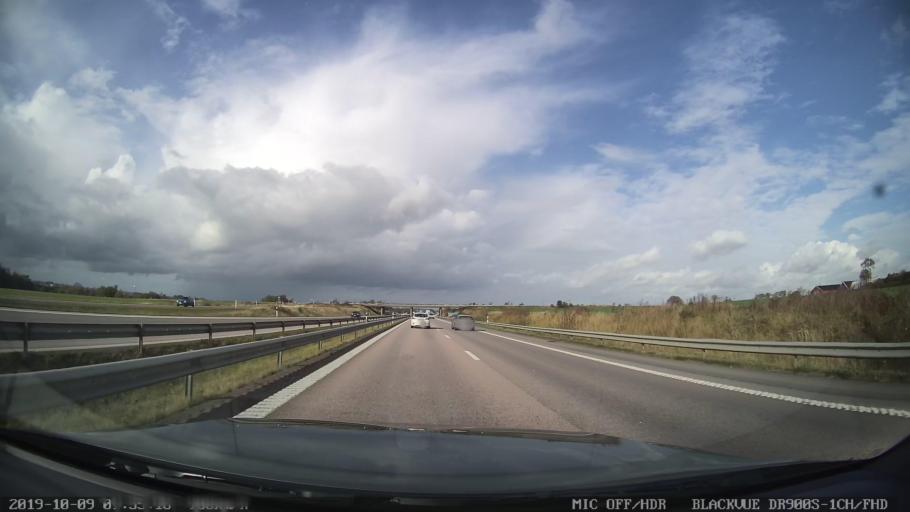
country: SE
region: Skane
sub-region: Helsingborg
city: Gantofta
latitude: 55.9639
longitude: 12.7980
